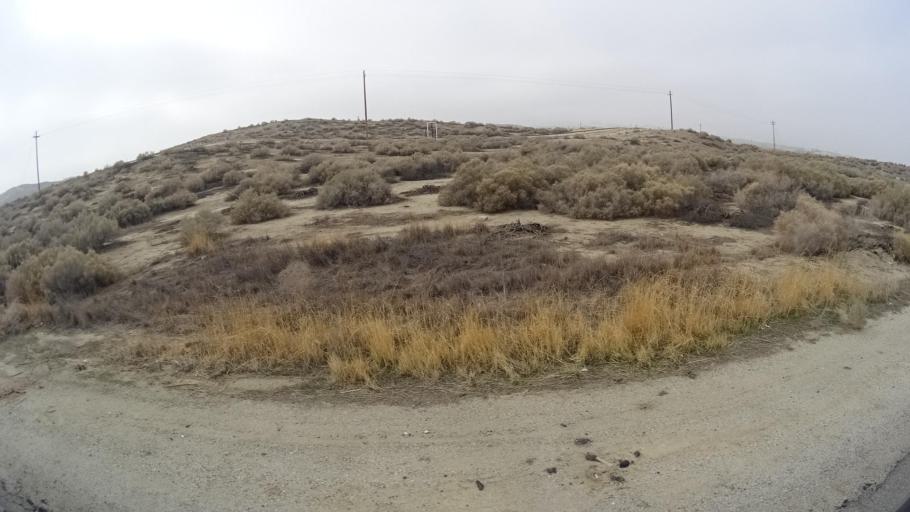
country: US
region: California
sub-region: Kern County
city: Maricopa
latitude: 35.0900
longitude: -119.4004
